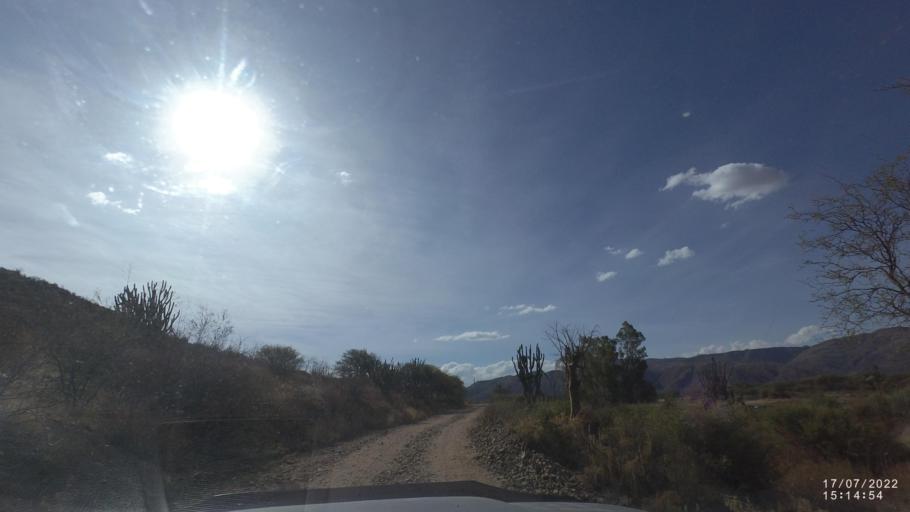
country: BO
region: Cochabamba
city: Capinota
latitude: -17.5593
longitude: -66.2610
